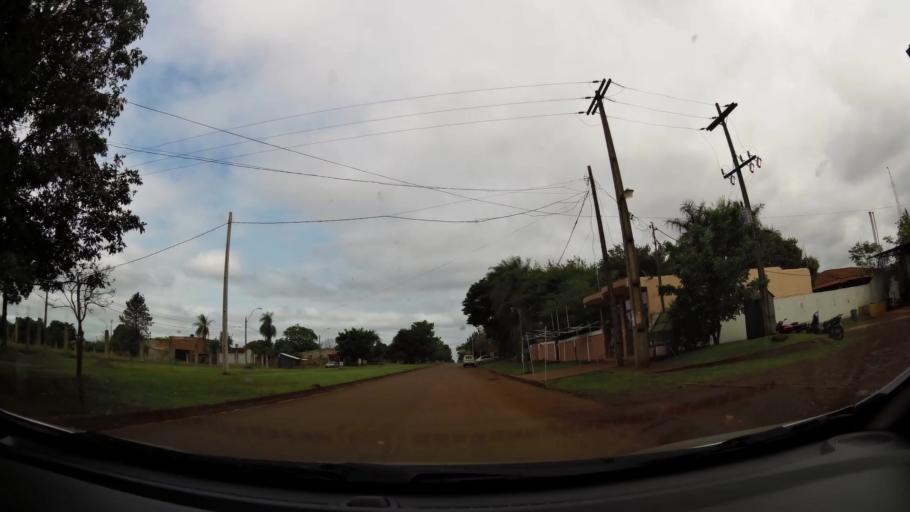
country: PY
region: Alto Parana
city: Ciudad del Este
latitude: -25.3797
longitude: -54.6512
